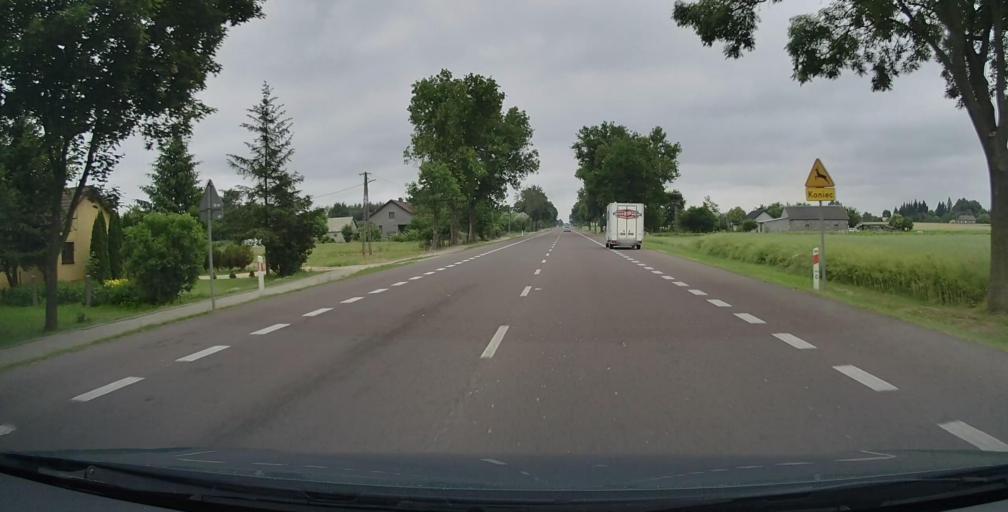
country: PL
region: Lublin Voivodeship
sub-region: Powiat bialski
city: Rzeczyca
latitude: 52.0386
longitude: 22.6922
